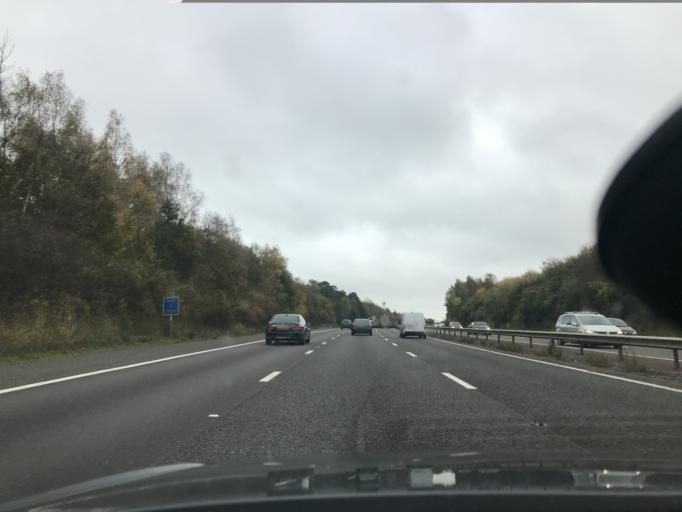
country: GB
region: England
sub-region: Warwickshire
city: Wroxall
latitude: 52.2890
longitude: -1.6694
